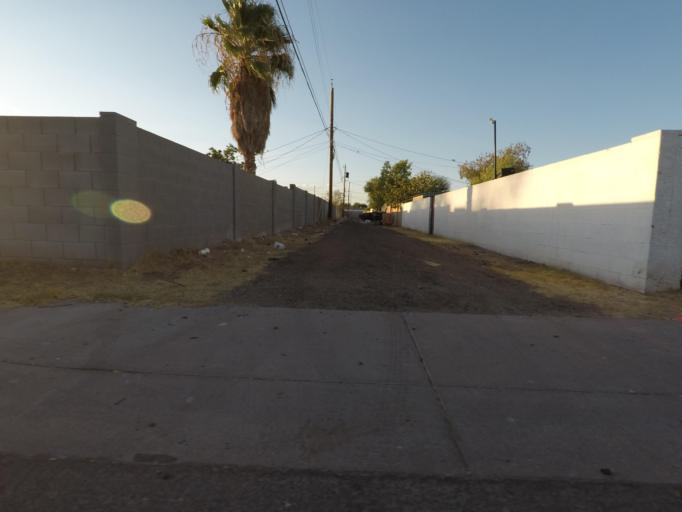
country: US
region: Arizona
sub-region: Maricopa County
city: Glendale
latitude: 33.5008
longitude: -112.1251
